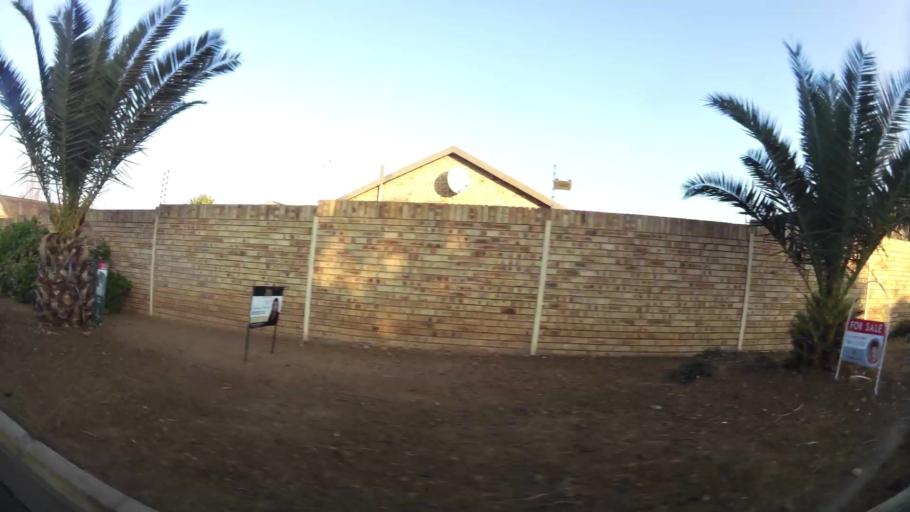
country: ZA
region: Orange Free State
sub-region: Mangaung Metropolitan Municipality
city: Bloemfontein
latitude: -29.1048
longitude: 26.1636
